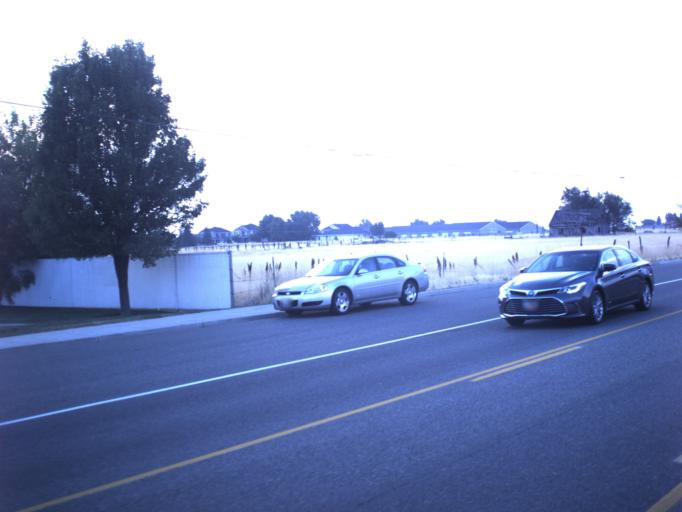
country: US
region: Utah
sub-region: Utah County
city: Mapleton
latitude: 40.1350
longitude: -111.5979
